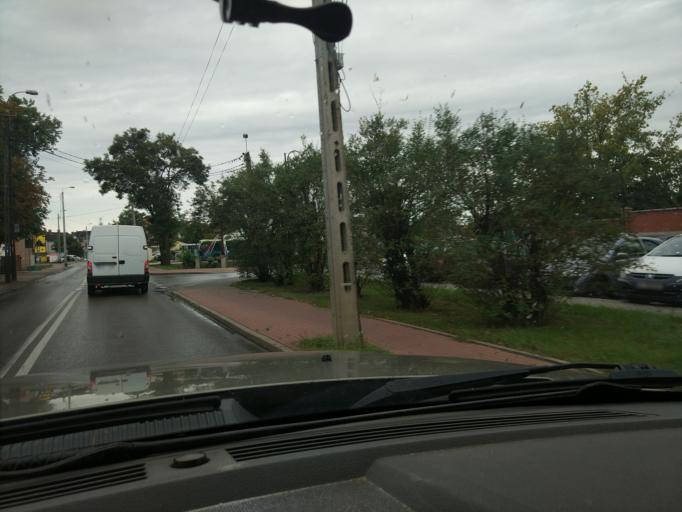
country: PL
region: Masovian Voivodeship
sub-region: Powiat pruszkowski
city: Brwinow
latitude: 52.1445
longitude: 20.7195
